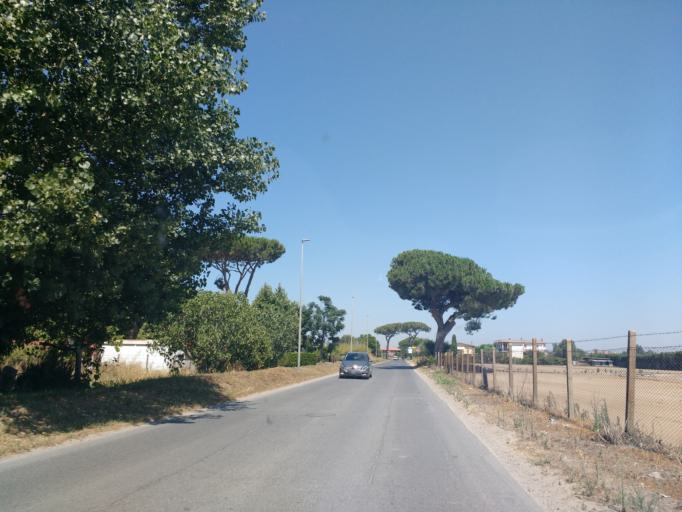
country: IT
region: Latium
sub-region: Citta metropolitana di Roma Capitale
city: Fregene
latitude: 41.8476
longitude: 12.2205
